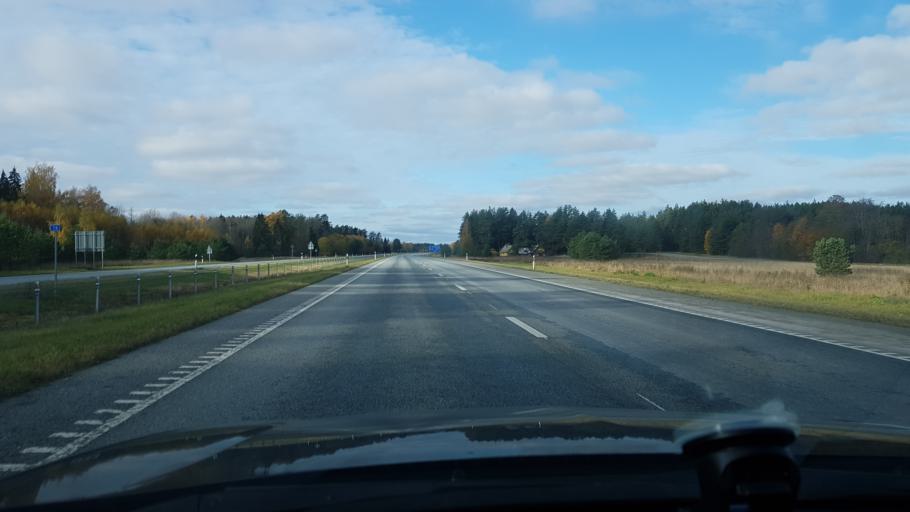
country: EE
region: Laeaene-Virumaa
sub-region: Kadrina vald
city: Kadrina
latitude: 59.4463
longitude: 26.0857
